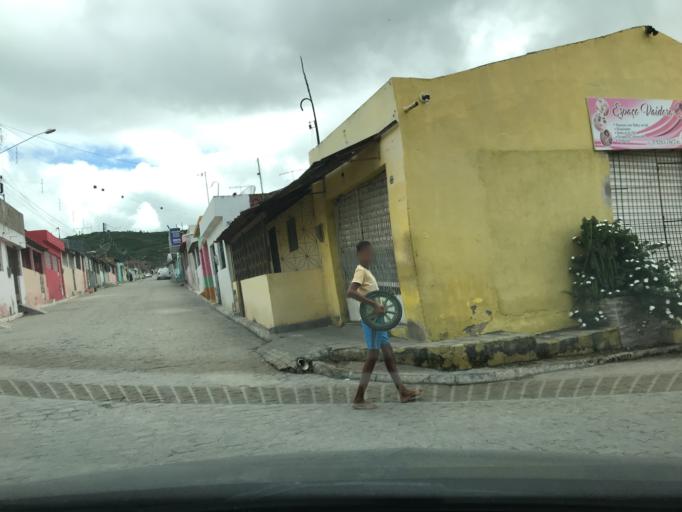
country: BR
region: Pernambuco
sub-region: Bezerros
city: Bezerros
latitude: -8.2311
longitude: -35.7618
